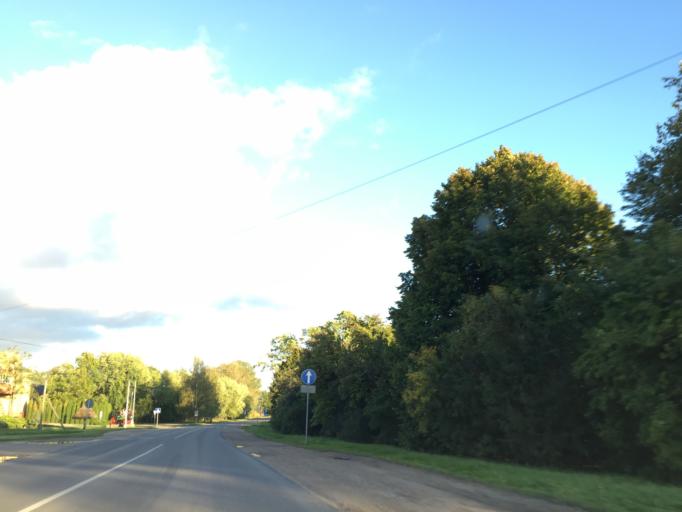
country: LV
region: Saldus Rajons
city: Saldus
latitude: 56.6933
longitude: 22.4452
